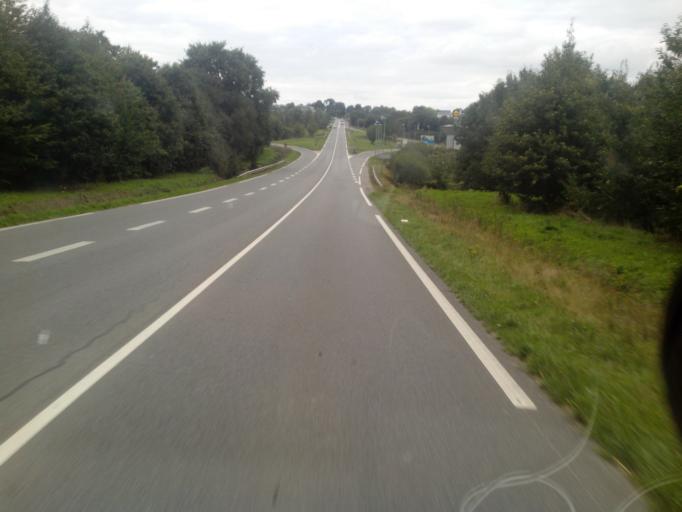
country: FR
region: Brittany
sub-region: Departement d'Ille-et-Vilaine
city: Melesse
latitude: 48.2102
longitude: -1.6991
